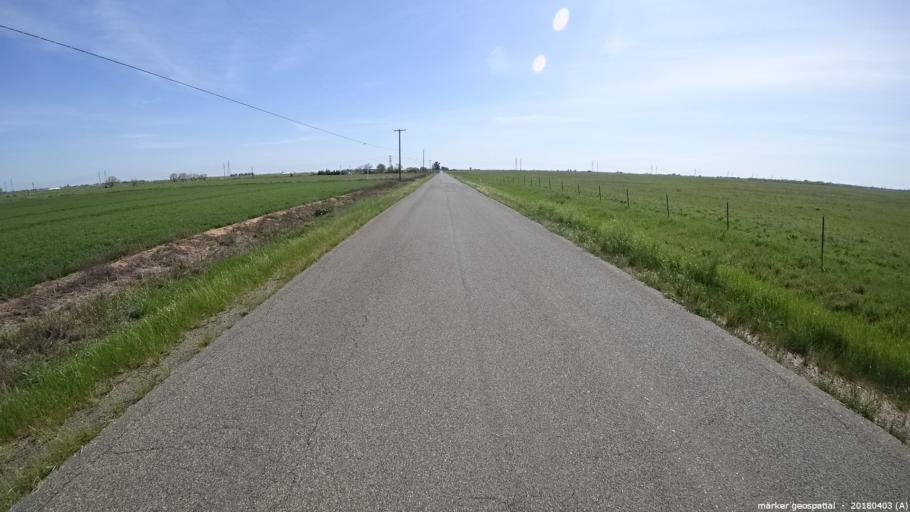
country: US
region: California
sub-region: Sacramento County
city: Wilton
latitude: 38.3595
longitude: -121.2976
